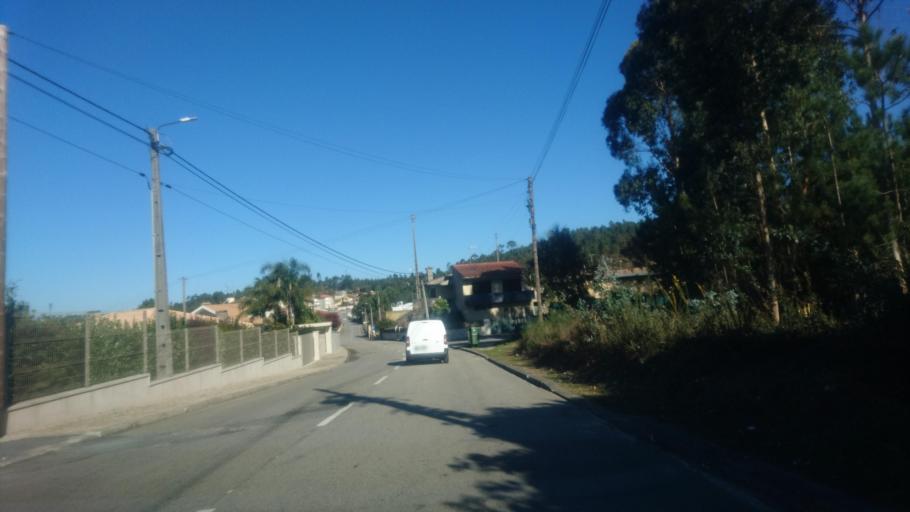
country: PT
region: Aveiro
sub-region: Oliveira de Azemeis
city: Sao Roque
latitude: 40.8769
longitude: -8.4646
